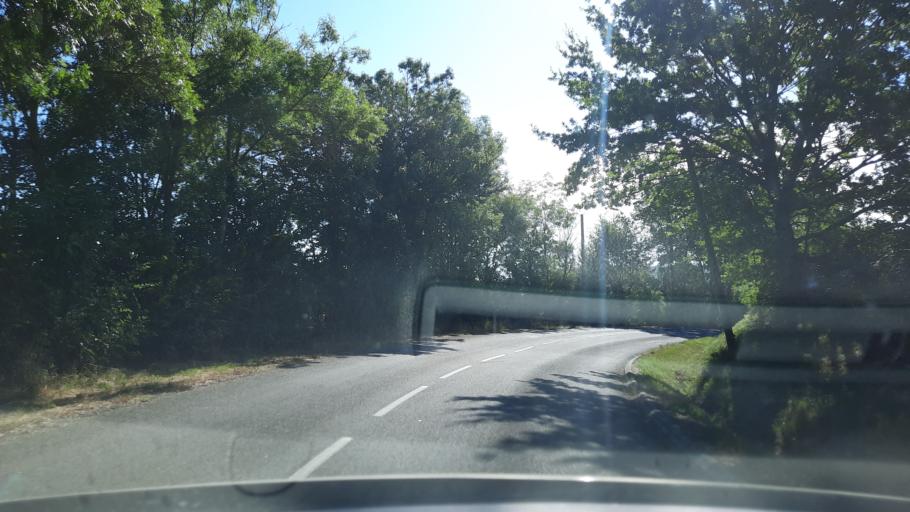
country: FR
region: Midi-Pyrenees
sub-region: Departement du Tarn-et-Garonne
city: Molieres
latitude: 44.1941
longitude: 1.4435
